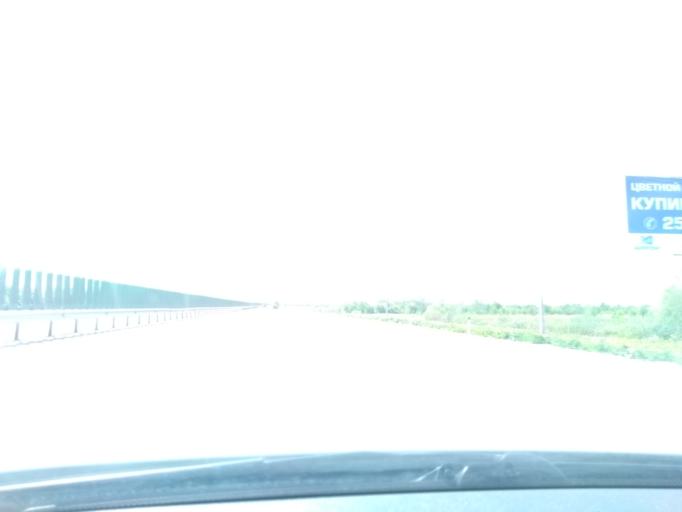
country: RU
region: Perm
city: Froly
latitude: 57.9313
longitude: 56.2000
